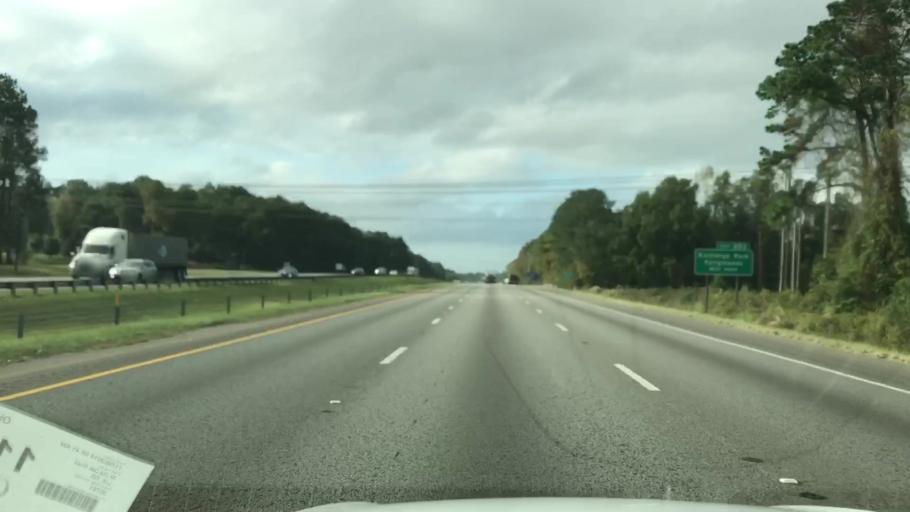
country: US
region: South Carolina
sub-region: Berkeley County
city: Ladson
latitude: 32.9898
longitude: -80.0845
